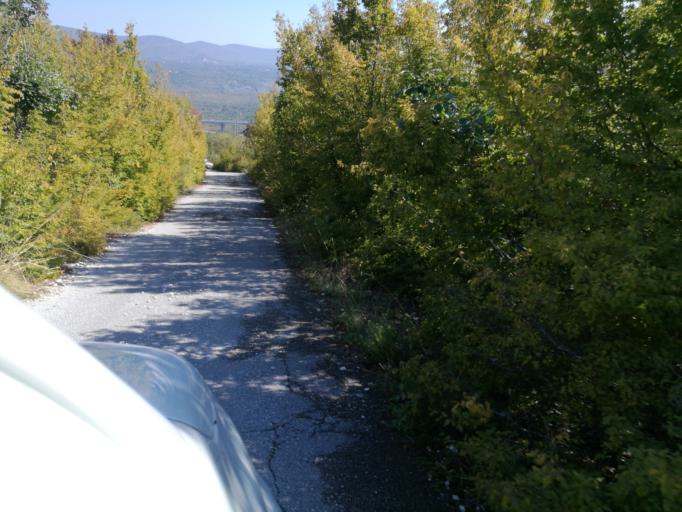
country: HR
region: Splitsko-Dalmatinska
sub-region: Grad Omis
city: Omis
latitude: 43.5168
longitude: 16.7279
